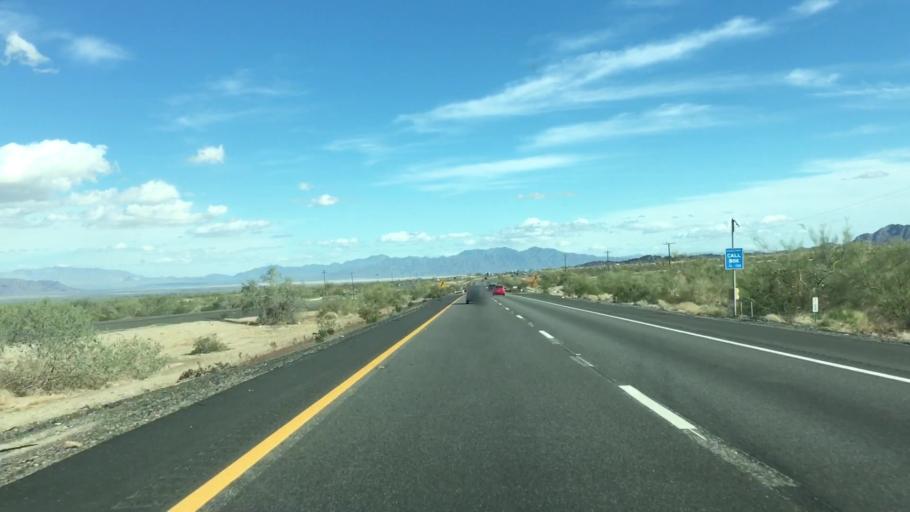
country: US
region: California
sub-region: Imperial County
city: Niland
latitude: 33.6986
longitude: -115.4696
